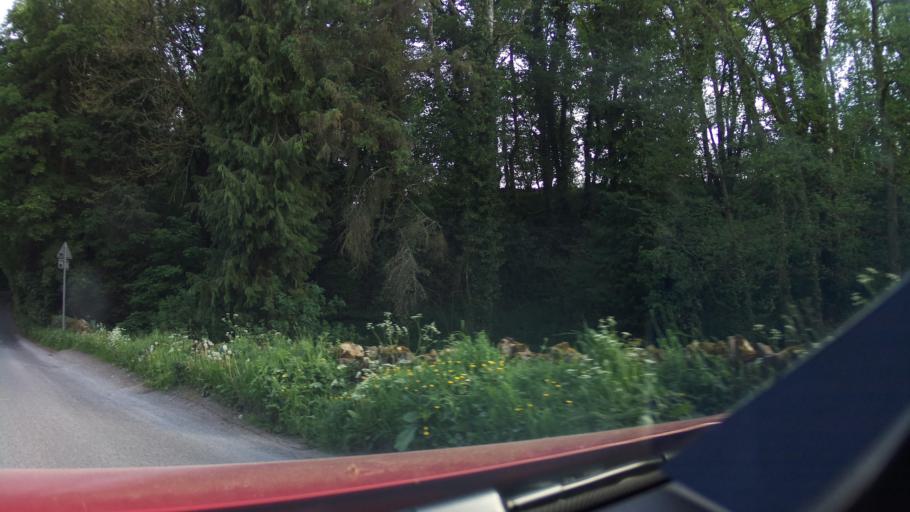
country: GB
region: England
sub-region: Gloucestershire
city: Westfield
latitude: 51.9145
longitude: -1.8531
